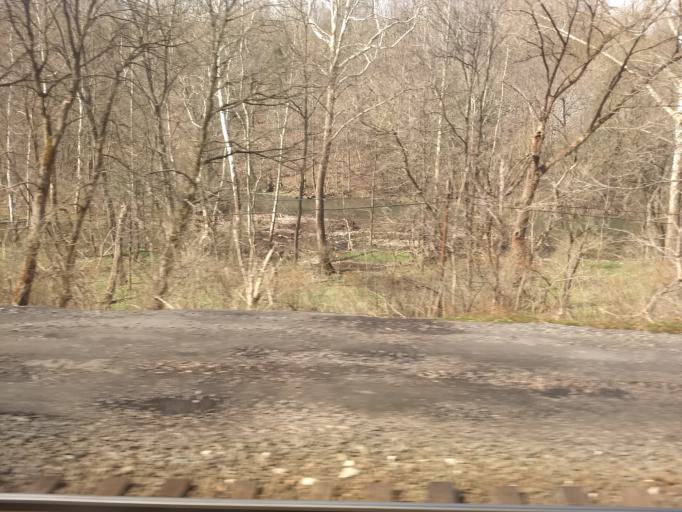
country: US
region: Pennsylvania
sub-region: Blair County
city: Tyrone
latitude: 40.6259
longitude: -78.1710
